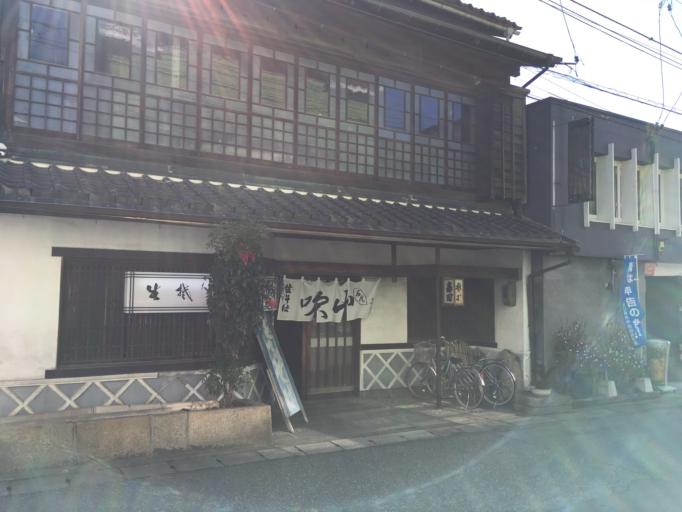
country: JP
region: Yamaguchi
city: Yamaguchi-shi
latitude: 34.1767
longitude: 131.4788
